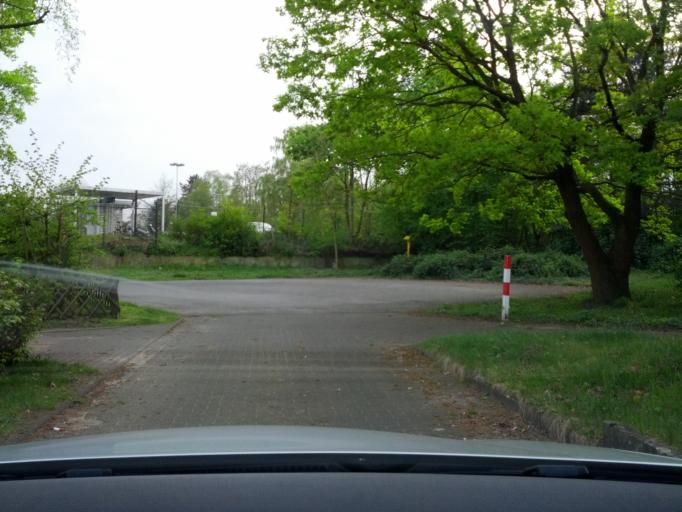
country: DE
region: North Rhine-Westphalia
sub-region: Regierungsbezirk Detmold
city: Guetersloh
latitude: 51.9086
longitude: 8.4074
